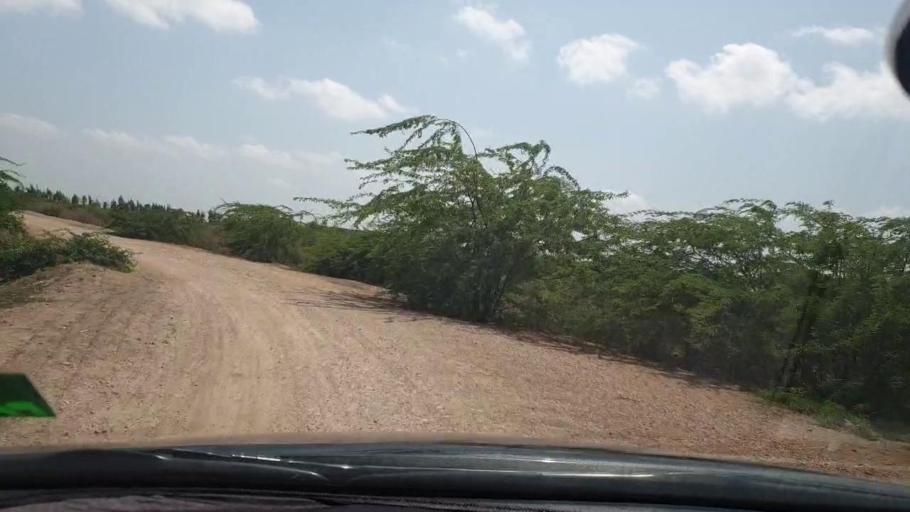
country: PK
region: Sindh
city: Tando Bago
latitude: 24.8682
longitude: 69.0871
